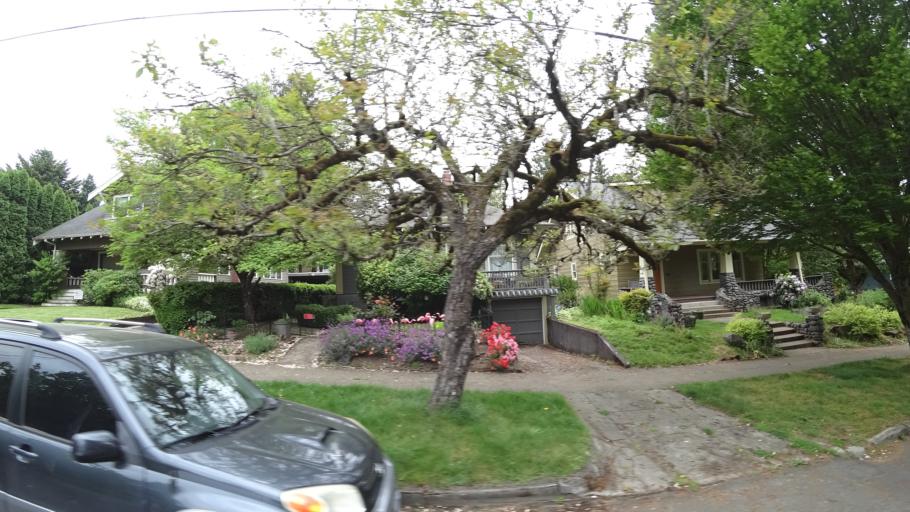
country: US
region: Oregon
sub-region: Multnomah County
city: Portland
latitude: 45.5388
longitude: -122.6099
